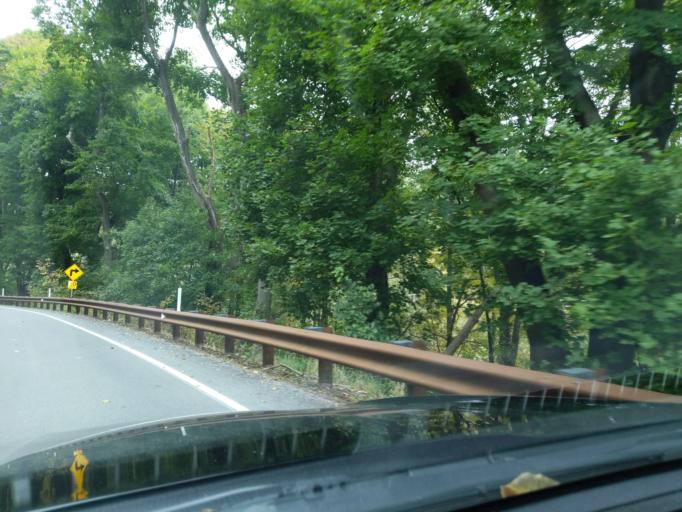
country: US
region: Pennsylvania
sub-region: Blair County
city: Altoona
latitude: 40.4949
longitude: -78.4626
